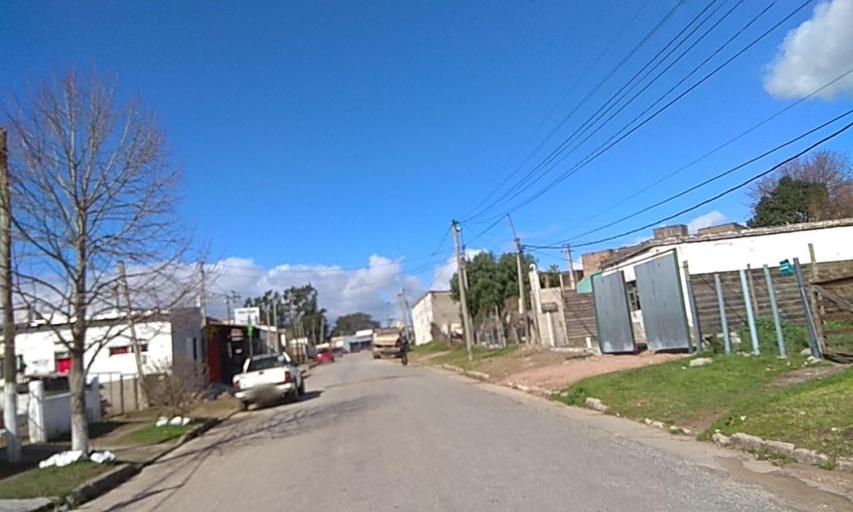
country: UY
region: Florida
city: Florida
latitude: -34.1067
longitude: -56.2097
